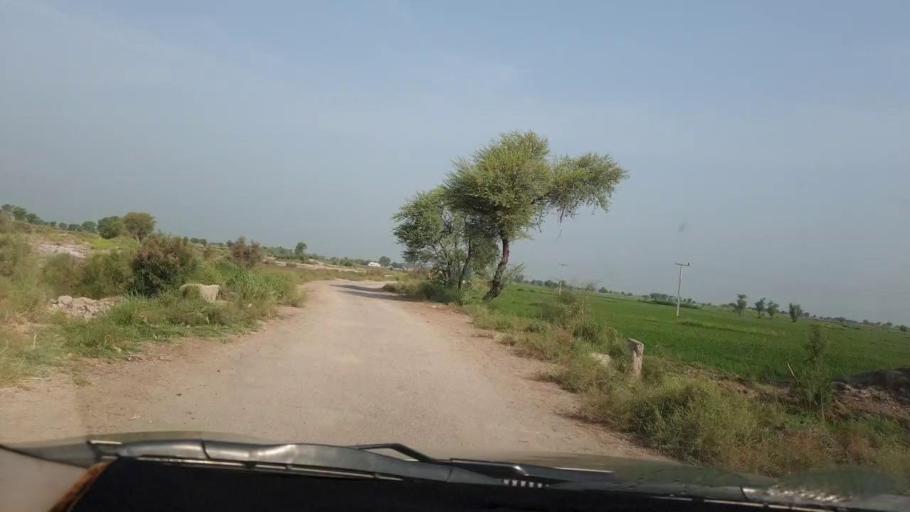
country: PK
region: Sindh
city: Goth Garelo
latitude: 27.4595
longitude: 68.0536
